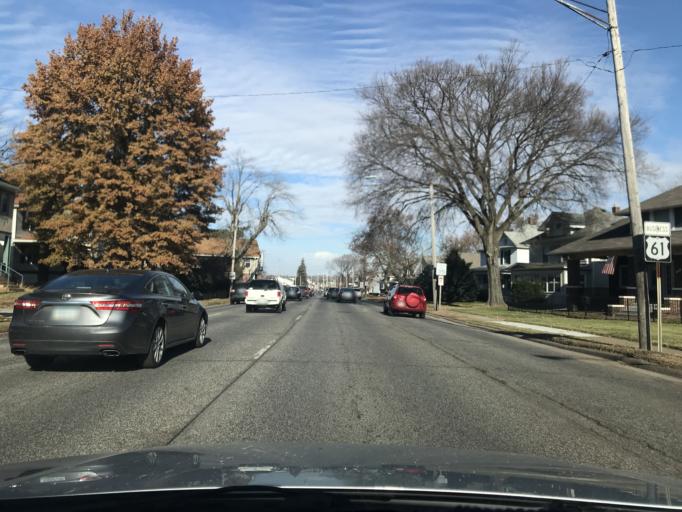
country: US
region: Iowa
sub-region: Scott County
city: Davenport
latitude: 41.5459
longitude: -90.5722
